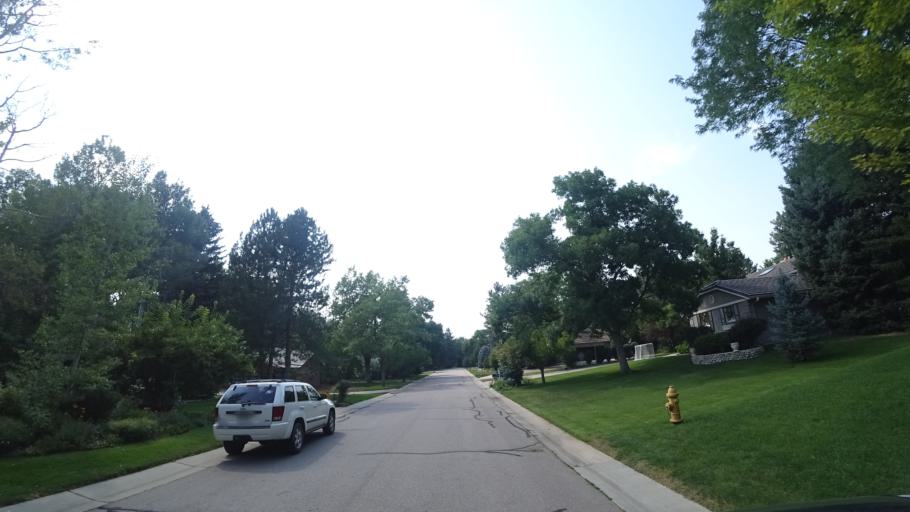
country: US
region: Colorado
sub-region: Arapahoe County
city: Greenwood Village
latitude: 39.6115
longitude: -104.9667
